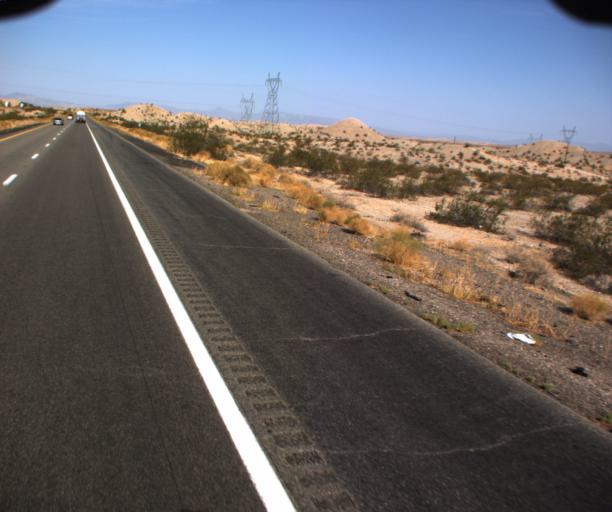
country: US
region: Arizona
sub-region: Mohave County
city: Desert Hills
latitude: 34.7276
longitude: -114.3824
